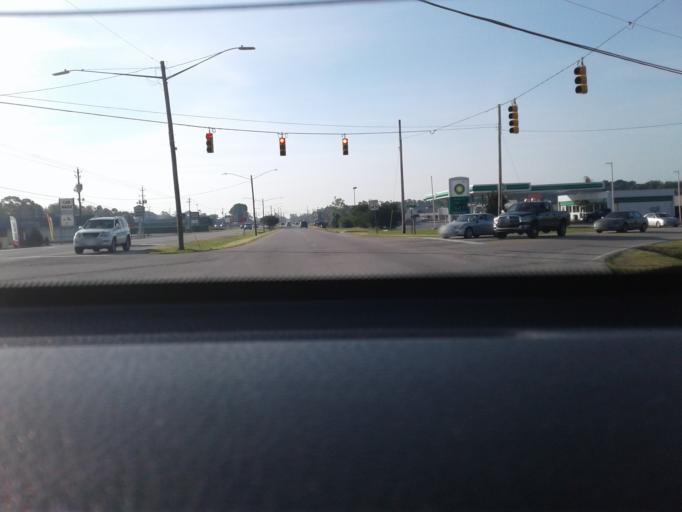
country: US
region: North Carolina
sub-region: Harnett County
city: Dunn
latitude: 35.3188
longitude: -78.6309
